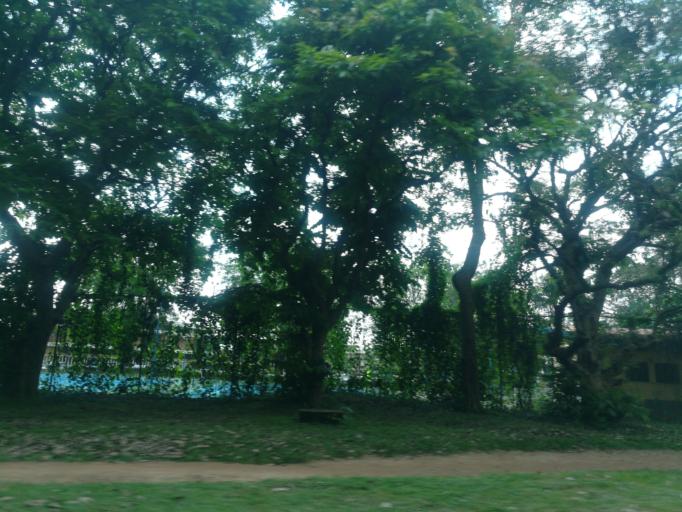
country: NG
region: Oyo
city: Ibadan
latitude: 7.4488
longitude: 3.9021
